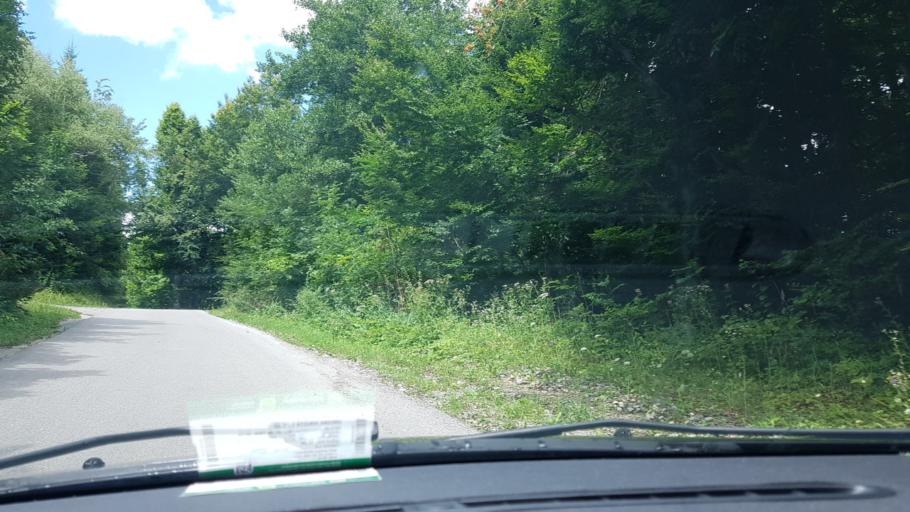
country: HR
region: Primorsko-Goranska
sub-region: Grad Delnice
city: Delnice
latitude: 45.3628
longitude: 14.7246
